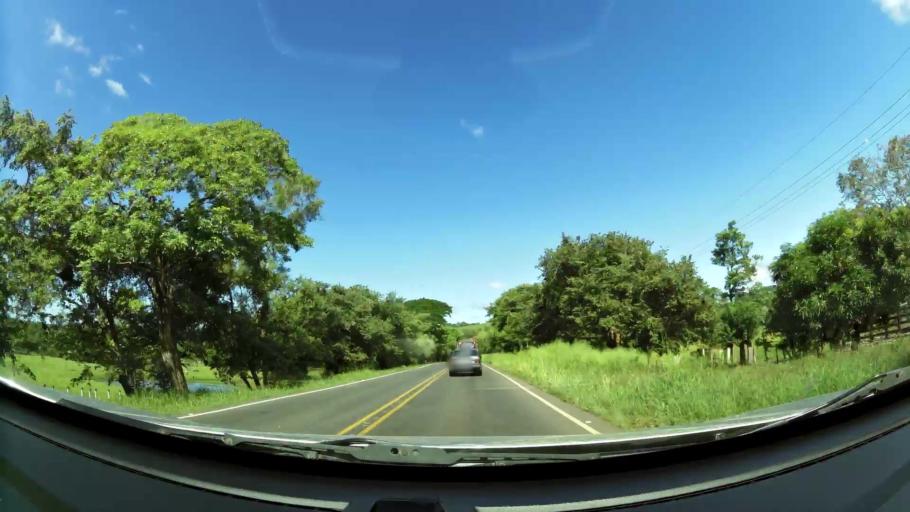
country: CR
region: Guanacaste
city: Juntas
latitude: 10.3165
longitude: -85.0449
